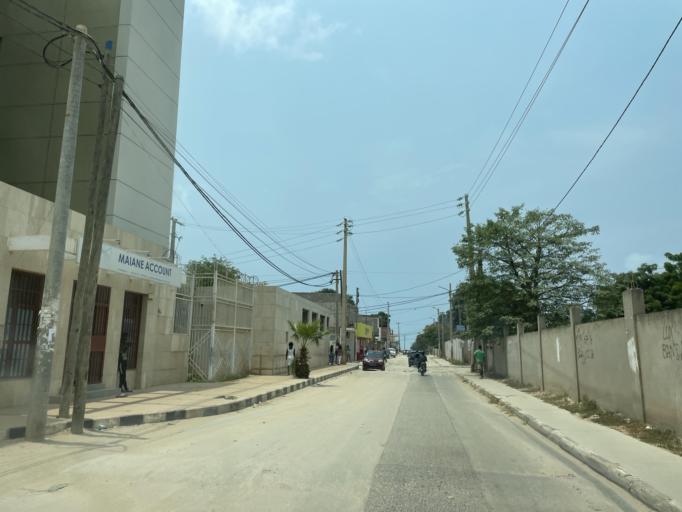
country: AO
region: Luanda
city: Luanda
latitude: -8.9412
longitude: 13.1646
